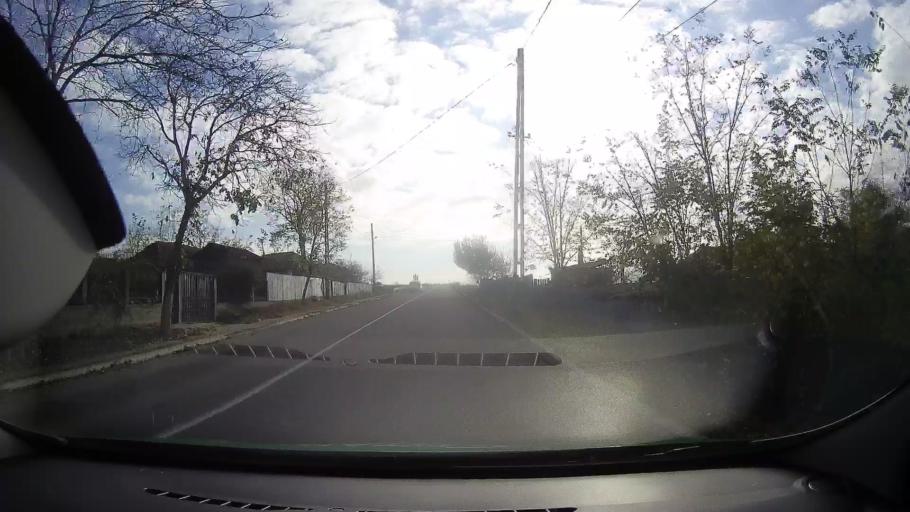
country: RO
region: Tulcea
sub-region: Comuna Bestepe
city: Bestepe
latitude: 45.0844
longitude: 29.0211
